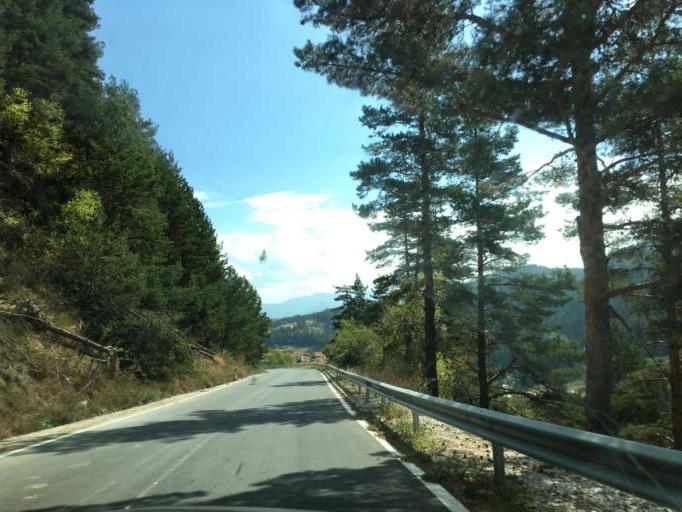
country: BG
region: Pazardzhik
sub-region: Obshtina Bratsigovo
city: Bratsigovo
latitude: 41.8856
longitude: 24.3435
